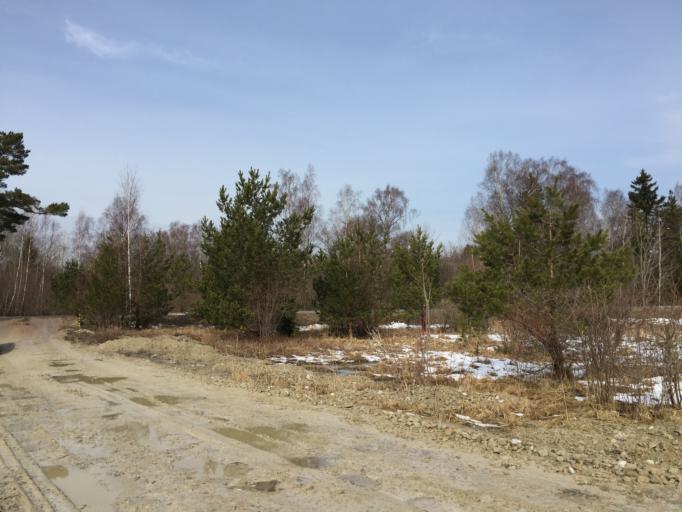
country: EE
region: Saare
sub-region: Kuressaare linn
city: Kuressaare
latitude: 58.3388
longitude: 22.4715
